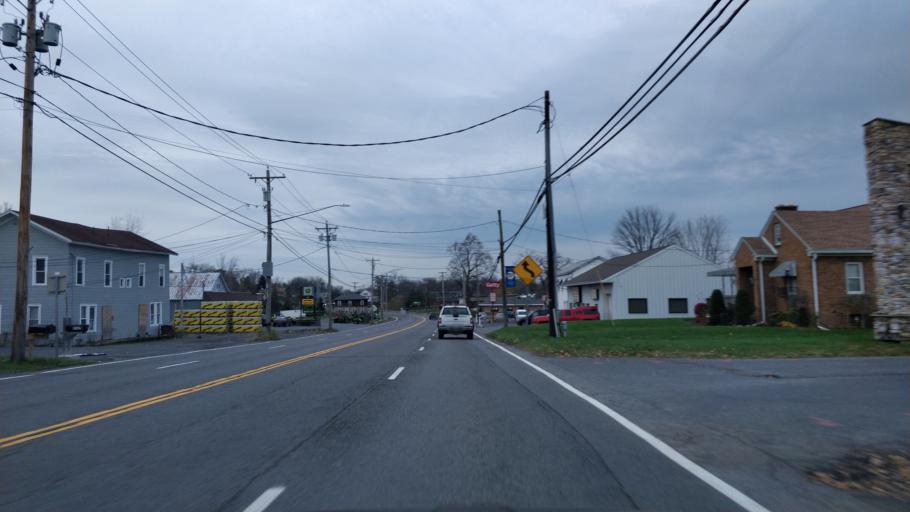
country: US
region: New York
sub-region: Onondaga County
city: North Syracuse
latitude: 43.1703
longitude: -76.1170
